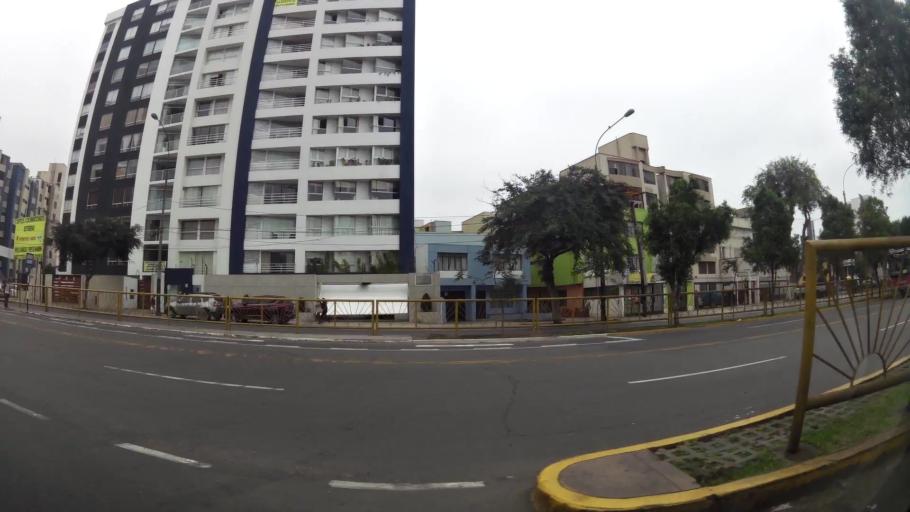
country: PE
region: Lima
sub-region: Lima
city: San Isidro
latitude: -12.0935
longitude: -77.0691
